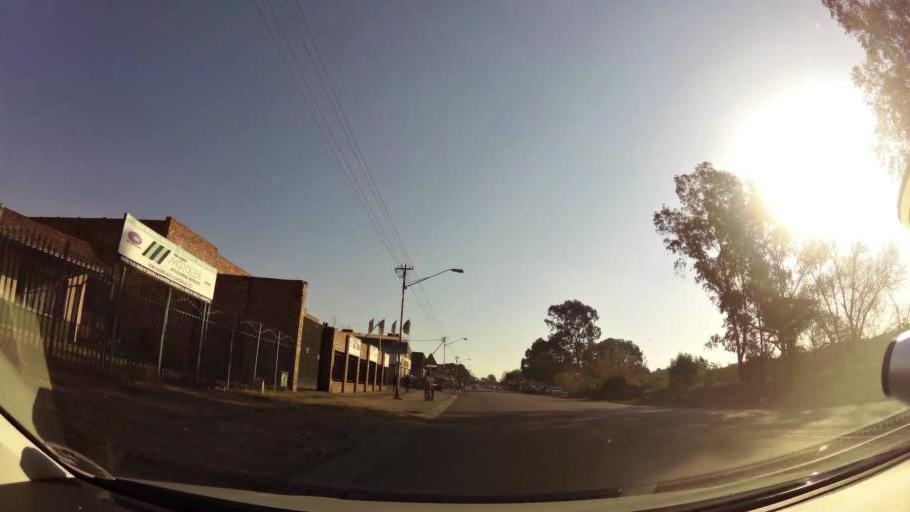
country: ZA
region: Gauteng
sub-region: City of Tshwane Metropolitan Municipality
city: Pretoria
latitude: -25.7438
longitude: 28.1575
